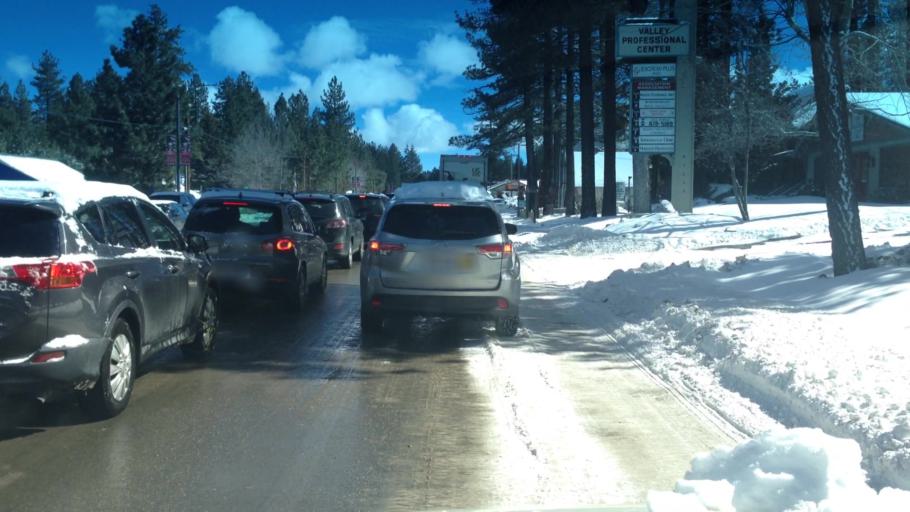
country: US
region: California
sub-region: San Bernardino County
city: Big Bear Lake
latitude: 34.2433
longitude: -116.8935
